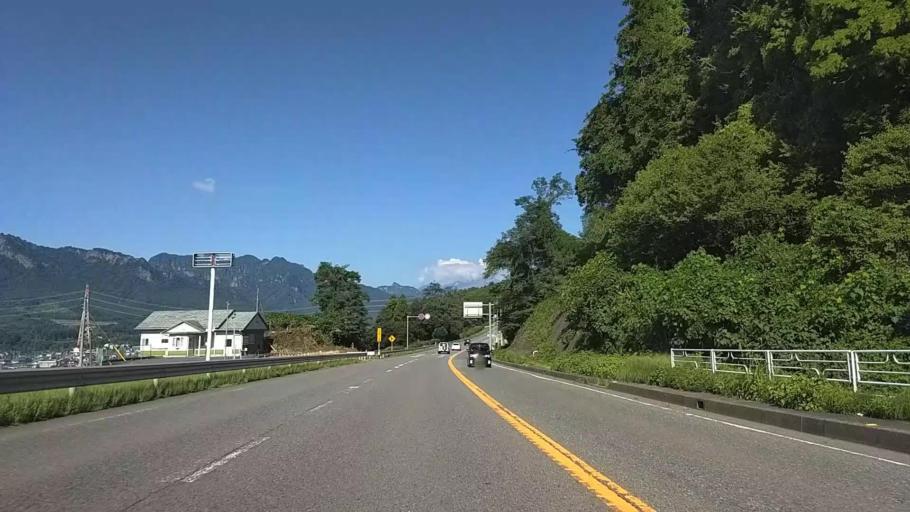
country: JP
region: Gunma
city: Annaka
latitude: 36.3175
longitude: 138.7983
